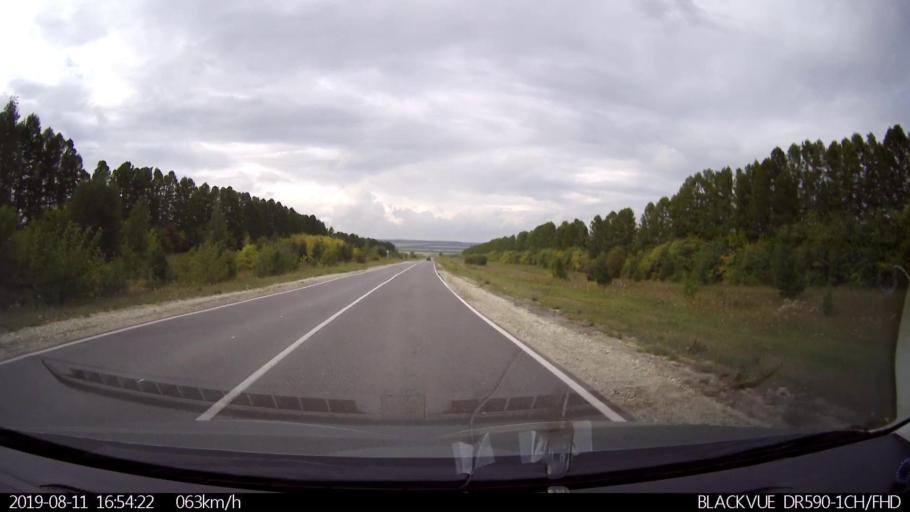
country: RU
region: Ulyanovsk
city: Mayna
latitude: 54.2720
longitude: 47.6665
